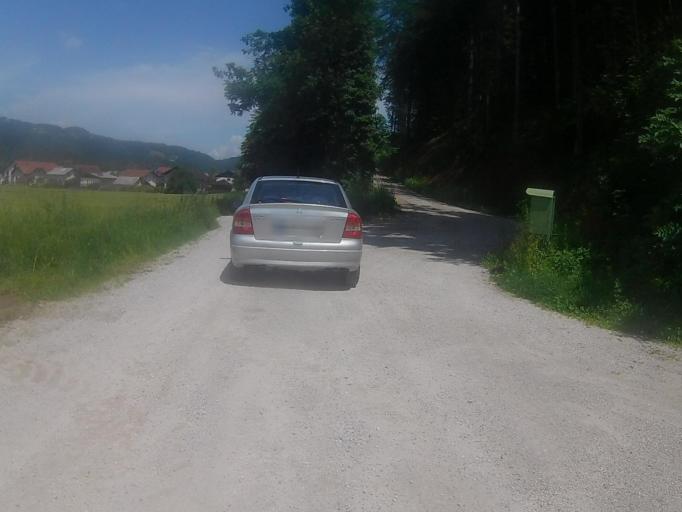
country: SI
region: Ruse
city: Bistrica ob Dravi
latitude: 46.5453
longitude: 15.5343
